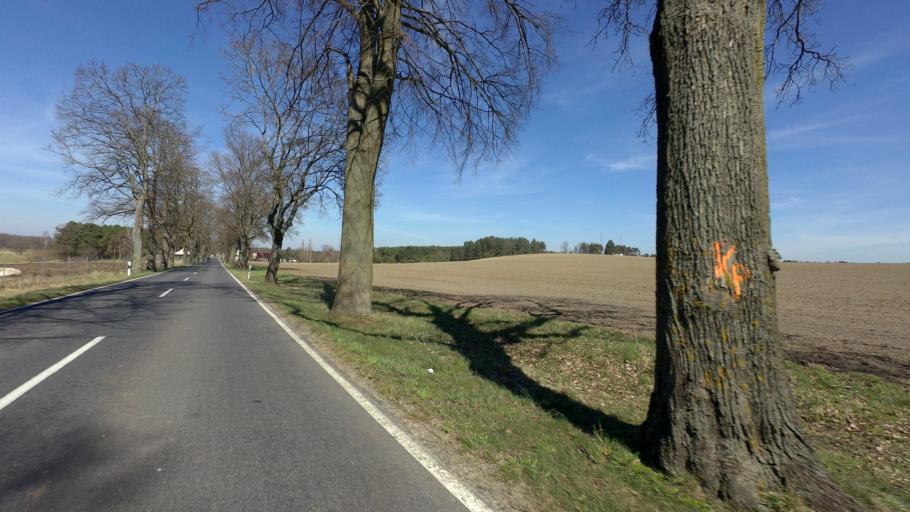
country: DE
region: Brandenburg
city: Storkow
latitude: 52.1877
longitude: 13.9184
